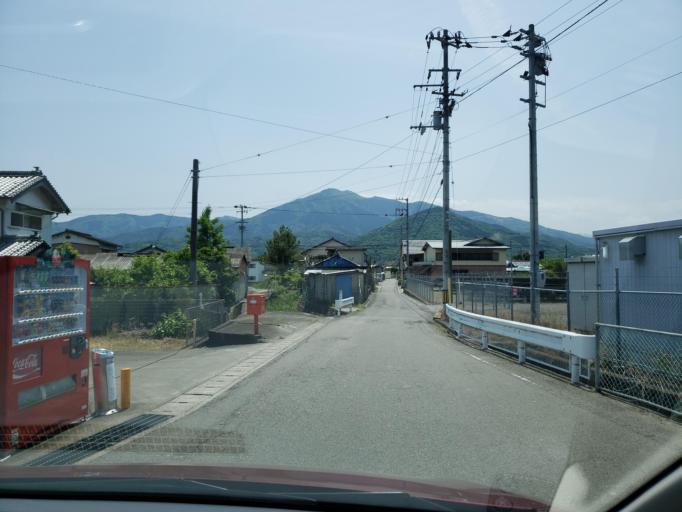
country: JP
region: Tokushima
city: Wakimachi
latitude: 34.0814
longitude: 134.1997
